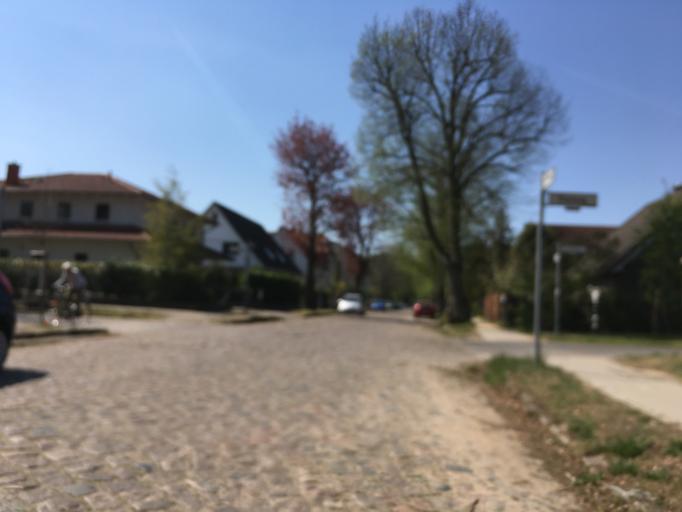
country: DE
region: Berlin
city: Buch
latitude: 52.6455
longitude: 13.5028
